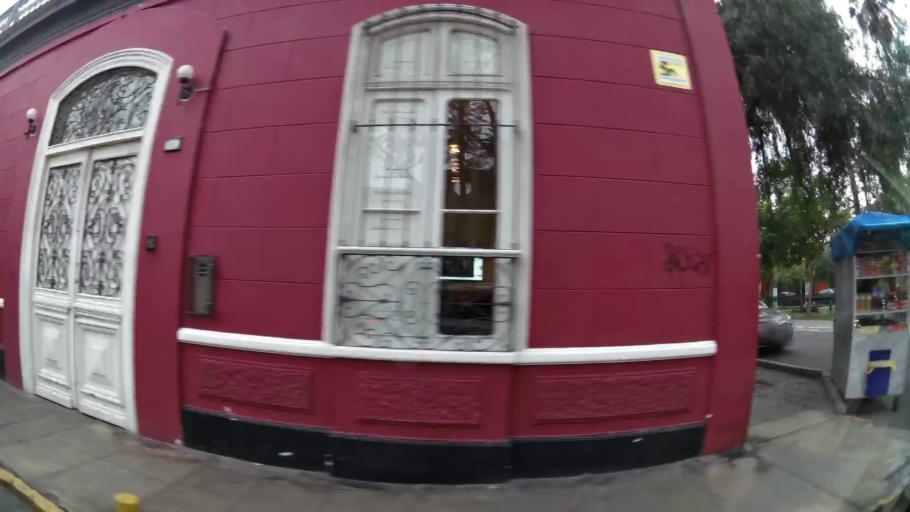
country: PE
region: Lima
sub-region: Lima
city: Surco
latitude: -12.1449
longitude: -77.0202
